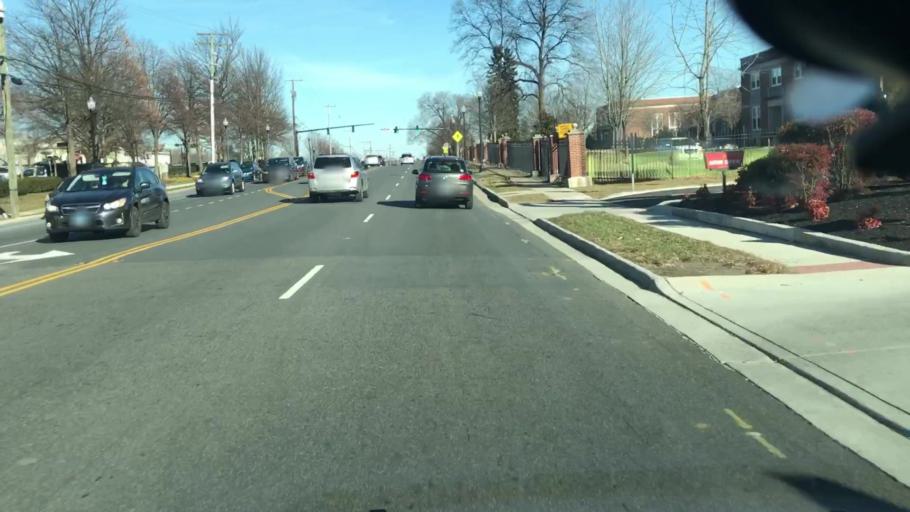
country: US
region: Virginia
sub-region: City of Fairfax
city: Fairfax
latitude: 38.8550
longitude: -77.3159
